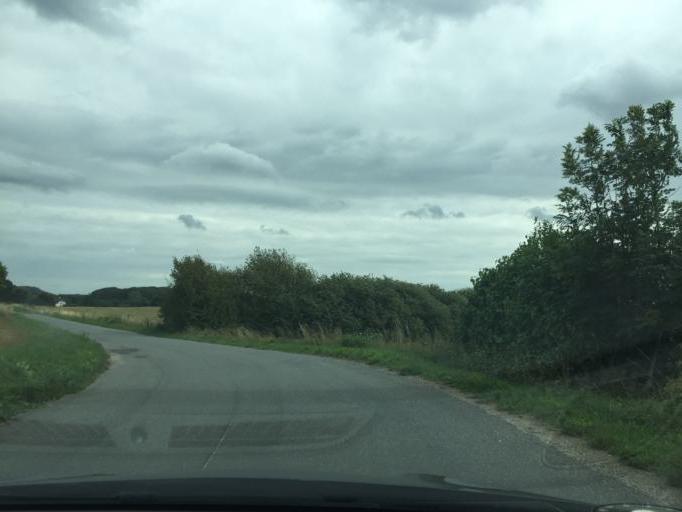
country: DK
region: South Denmark
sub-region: Assens Kommune
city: Arup
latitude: 55.3783
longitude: 10.0664
